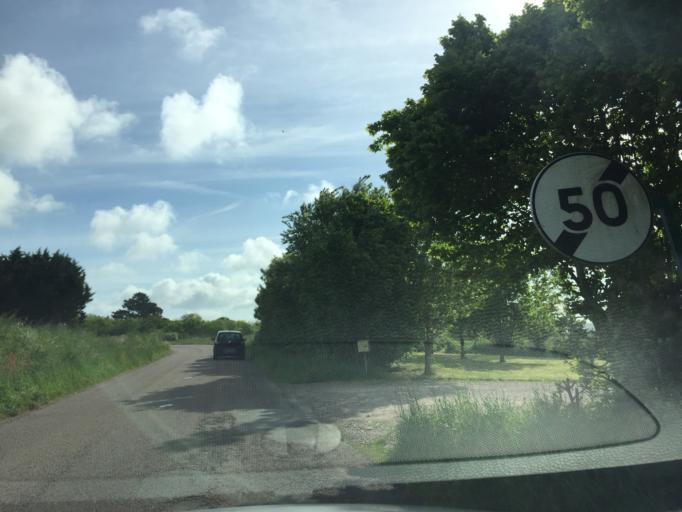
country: FR
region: Brittany
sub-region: Departement des Cotes-d'Armor
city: Matignon
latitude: 48.6286
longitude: -2.3316
